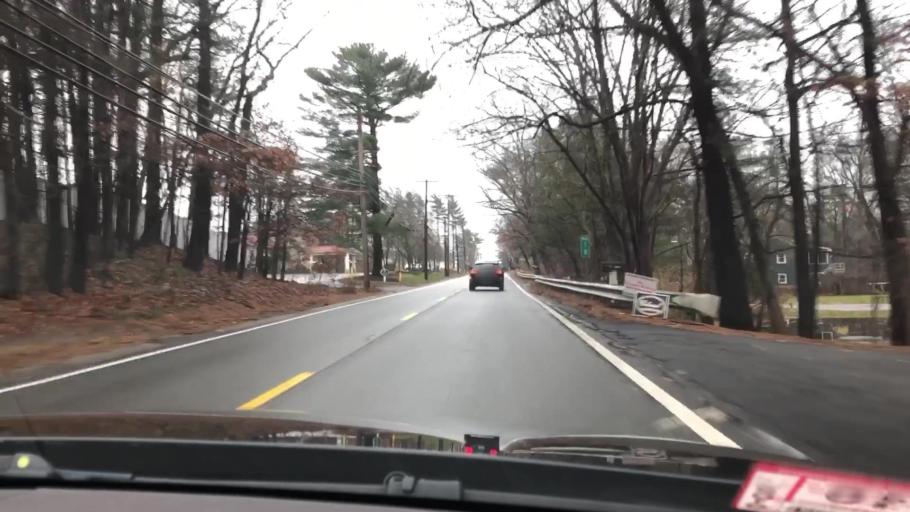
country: US
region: Massachusetts
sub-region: Norfolk County
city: Walpole
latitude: 42.1253
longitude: -71.2697
